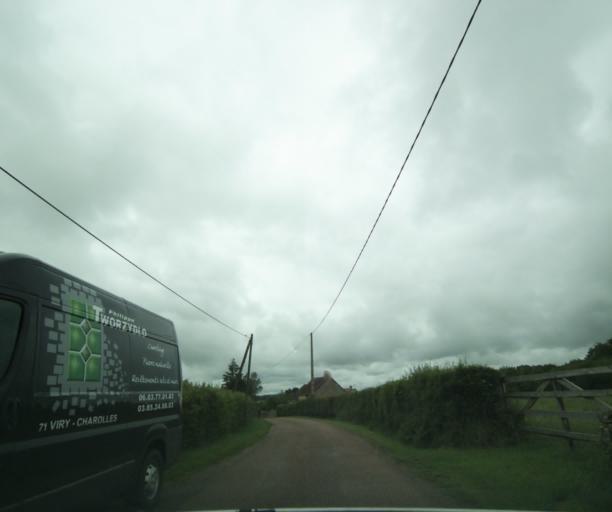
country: FR
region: Bourgogne
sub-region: Departement de Saone-et-Loire
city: Charolles
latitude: 46.4660
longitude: 4.3677
